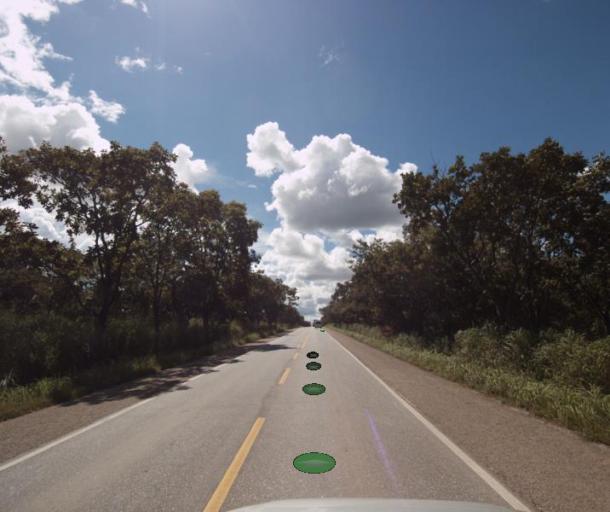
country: BR
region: Goias
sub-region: Porangatu
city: Porangatu
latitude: -13.6647
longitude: -49.0316
